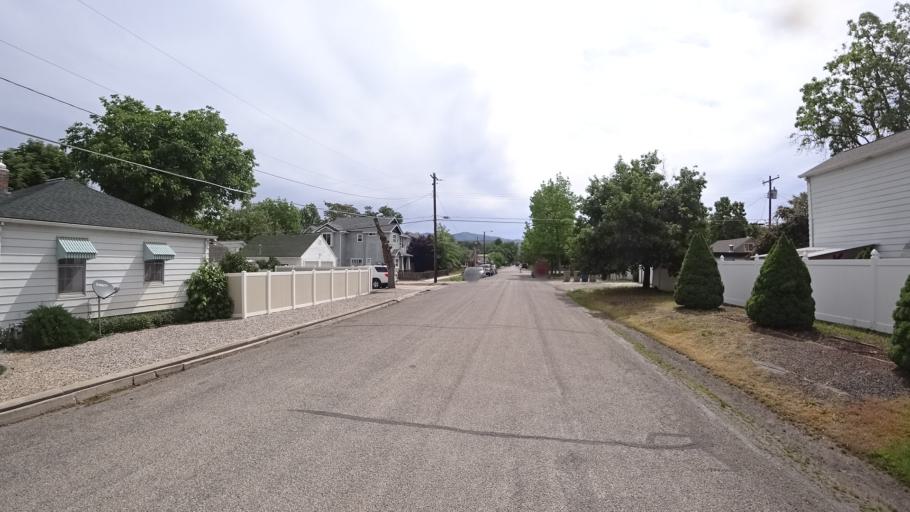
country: US
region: Idaho
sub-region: Ada County
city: Boise
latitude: 43.5907
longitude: -116.1998
